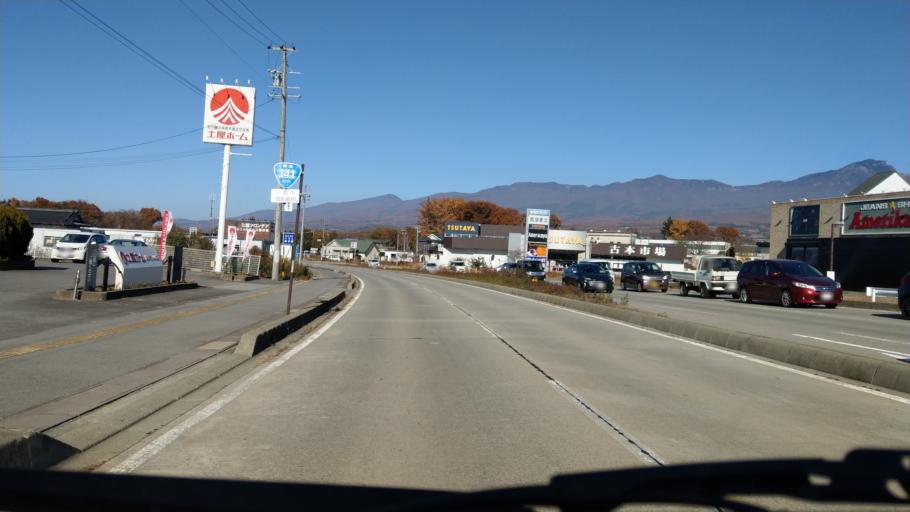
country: JP
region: Nagano
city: Komoro
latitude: 36.2997
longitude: 138.4673
